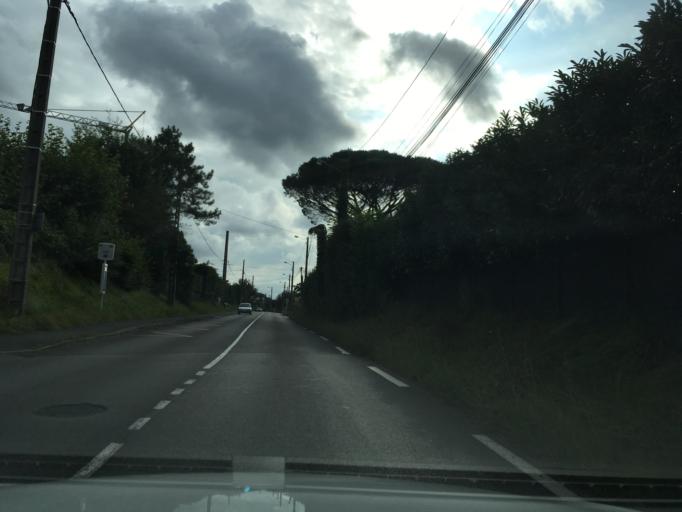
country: FR
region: Aquitaine
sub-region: Departement des Pyrenees-Atlantiques
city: Bassussarry
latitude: 43.4560
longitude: -1.5091
